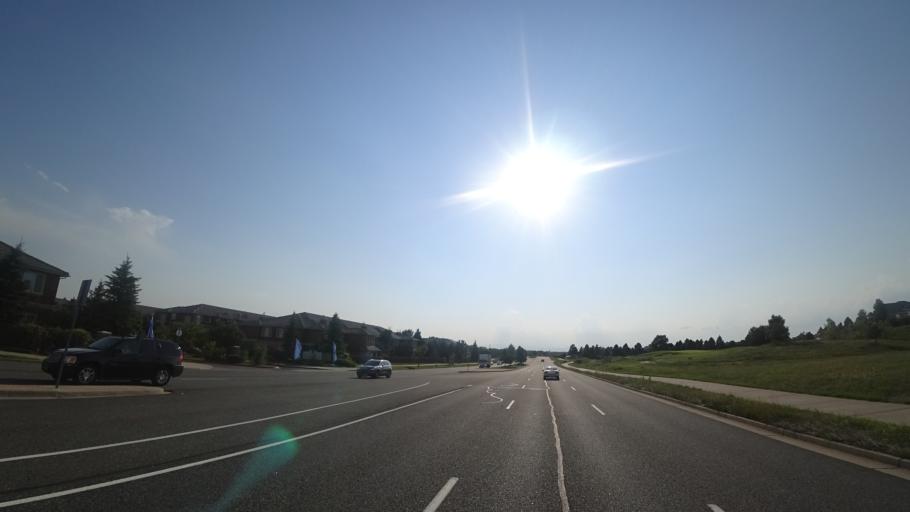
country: US
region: Colorado
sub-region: Douglas County
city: Parker
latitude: 39.5950
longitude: -104.7326
